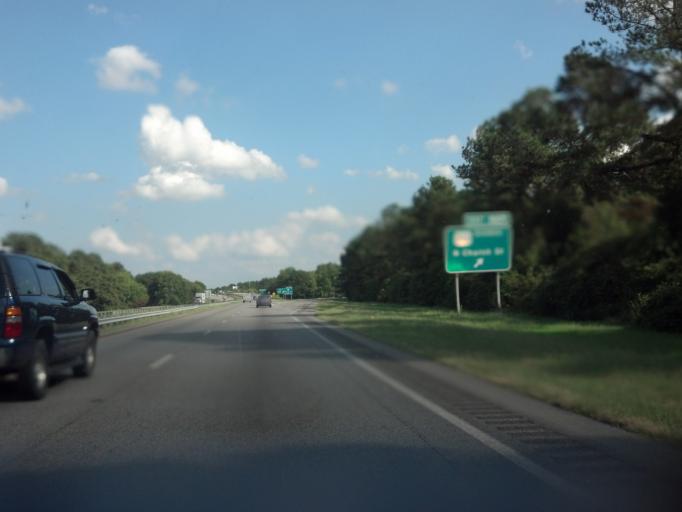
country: US
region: North Carolina
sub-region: Nash County
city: Rocky Mount
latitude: 35.9628
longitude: -77.7976
